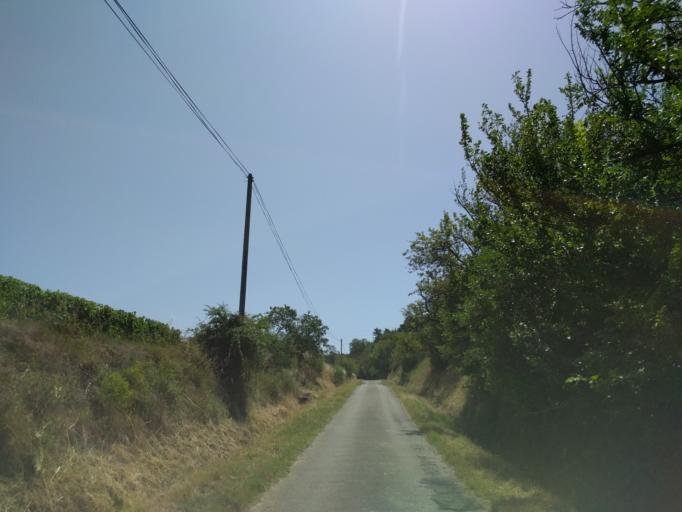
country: FR
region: Languedoc-Roussillon
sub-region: Departement de l'Aude
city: Cazilhac
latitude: 43.1989
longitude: 2.3763
